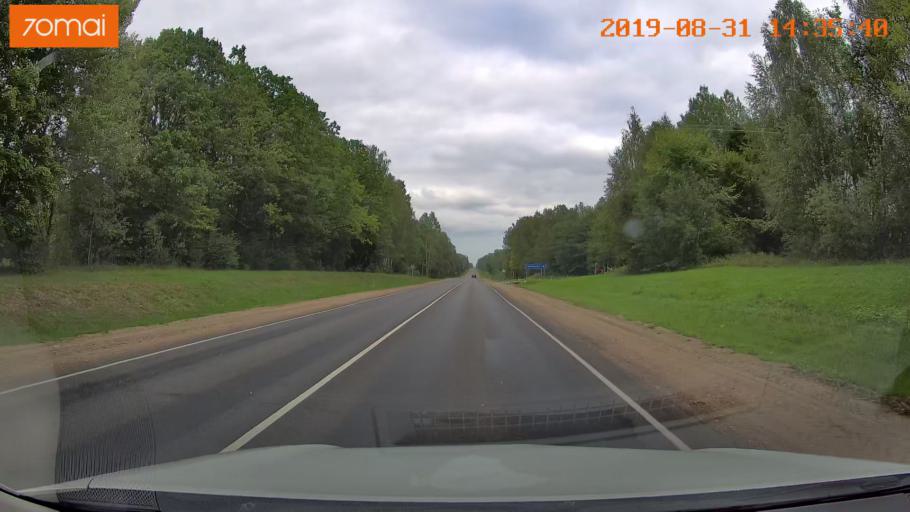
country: RU
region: Smolensk
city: Yekimovichi
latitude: 54.1645
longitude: 33.4612
